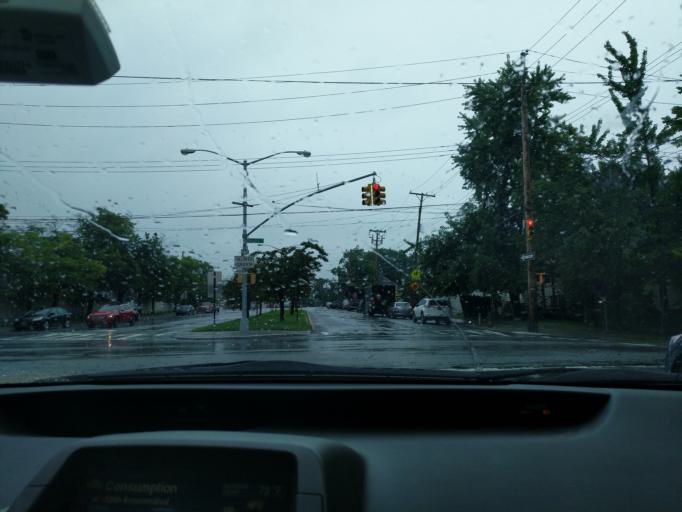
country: US
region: New York
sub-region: Richmond County
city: Bloomfield
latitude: 40.6305
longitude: -74.1440
